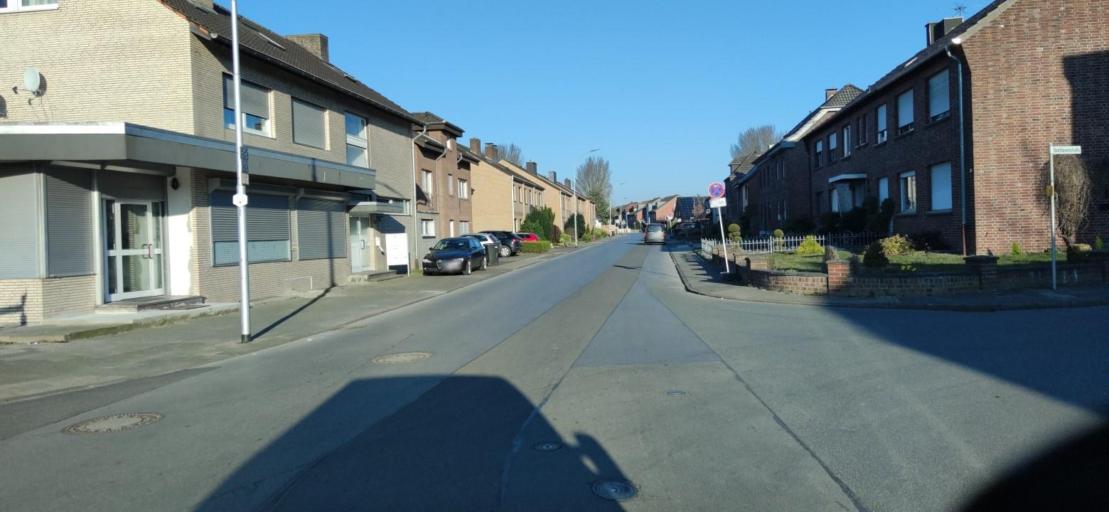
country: DE
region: North Rhine-Westphalia
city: Straelen
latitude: 51.4368
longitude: 6.2614
